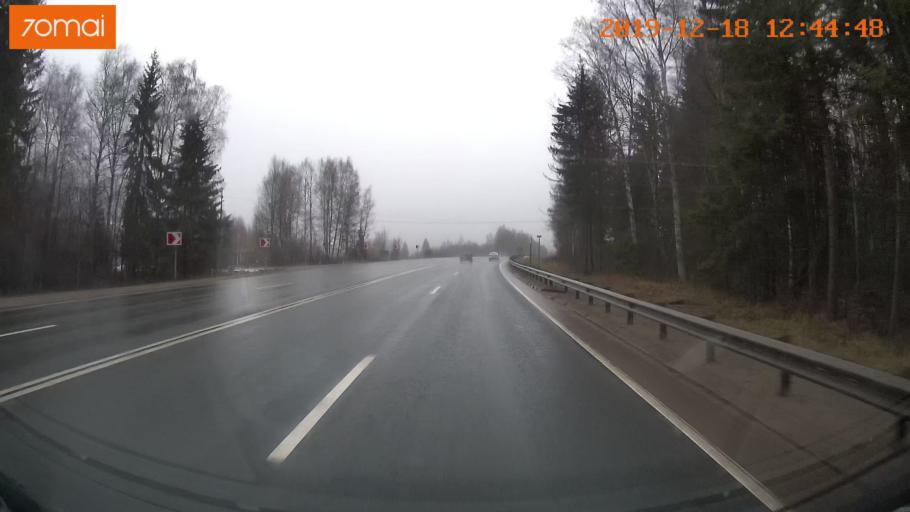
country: RU
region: Moskovskaya
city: Klin
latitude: 56.2242
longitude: 36.6510
